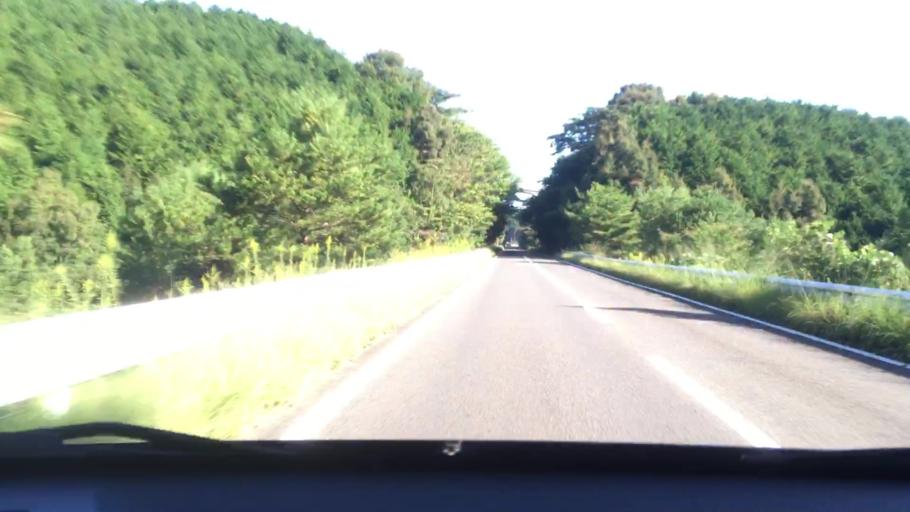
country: JP
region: Nagasaki
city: Sasebo
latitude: 33.0006
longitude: 129.7074
